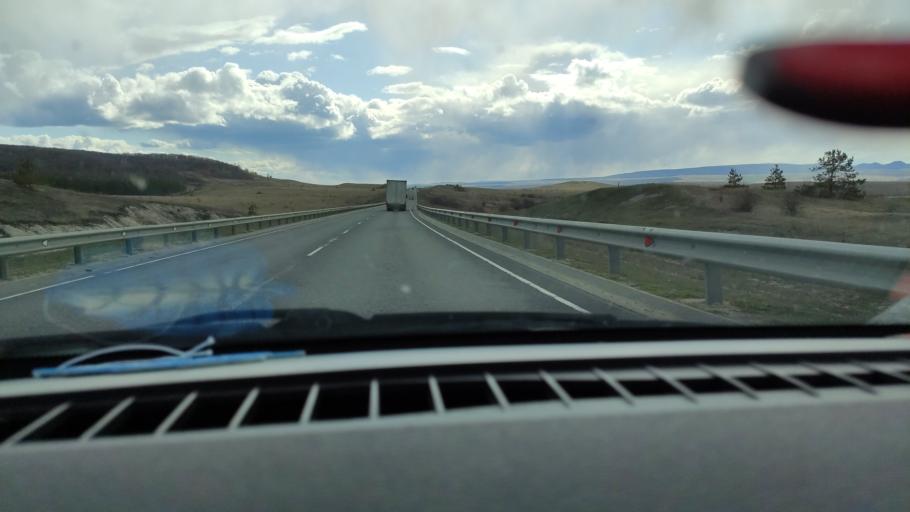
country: RU
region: Saratov
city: Alekseyevka
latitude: 52.3639
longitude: 47.9585
